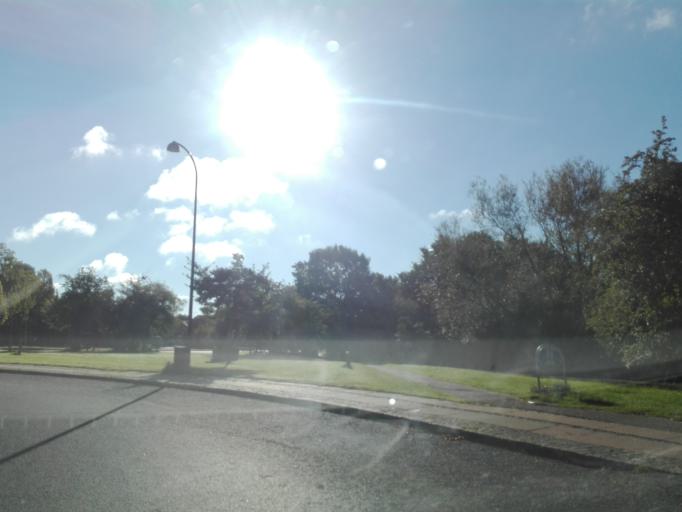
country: DK
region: Capital Region
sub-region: Lyngby-Tarbaek Kommune
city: Kongens Lyngby
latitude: 55.7468
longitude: 12.5215
